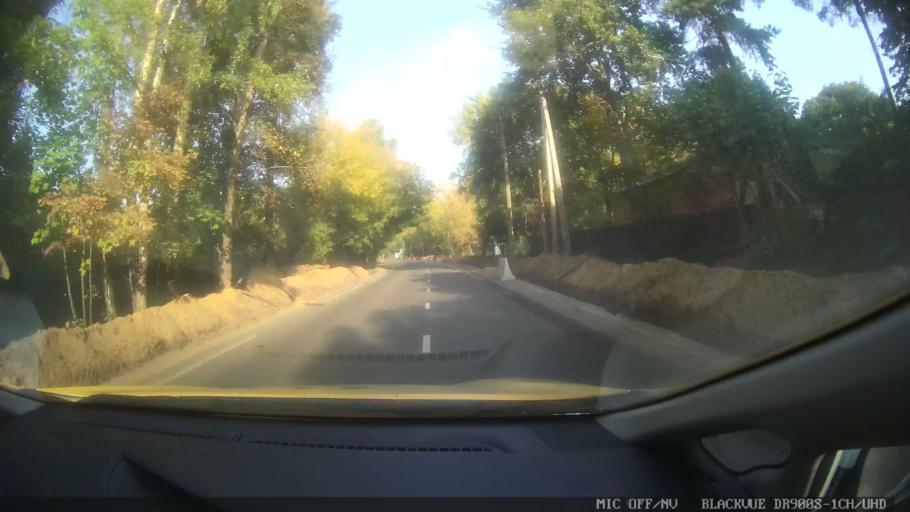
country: RU
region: Moscow
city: Zhulebino
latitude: 55.7033
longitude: 37.8595
